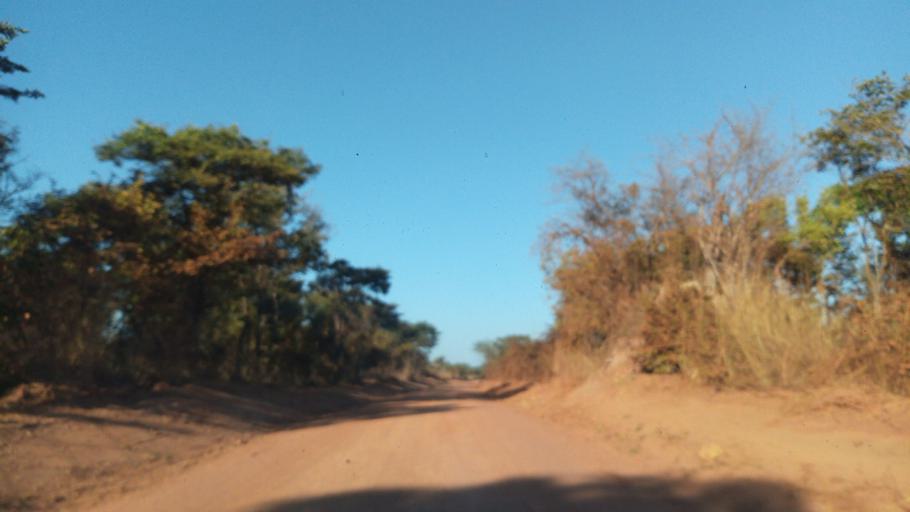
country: ZM
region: Luapula
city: Mwense
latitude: -10.4752
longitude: 28.5135
